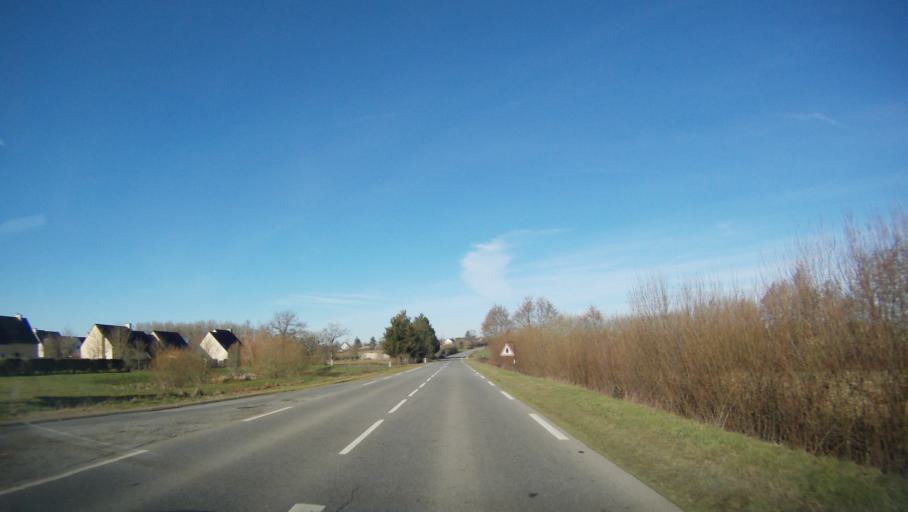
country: FR
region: Brittany
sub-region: Departement d'Ille-et-Vilaine
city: Bourgbarre
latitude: 47.9982
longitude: -1.6233
